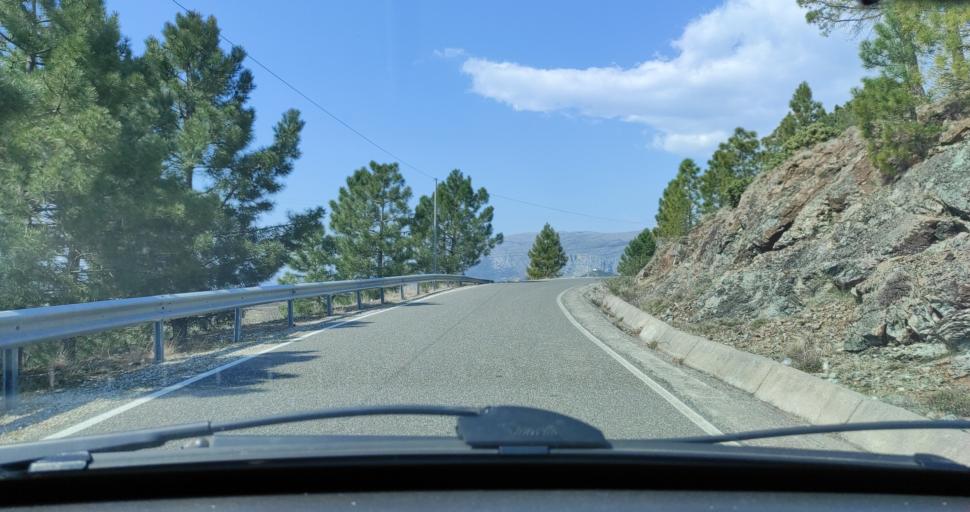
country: AL
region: Shkoder
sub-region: Rrethi i Shkodres
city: Hajmel
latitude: 41.9826
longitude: 19.6443
